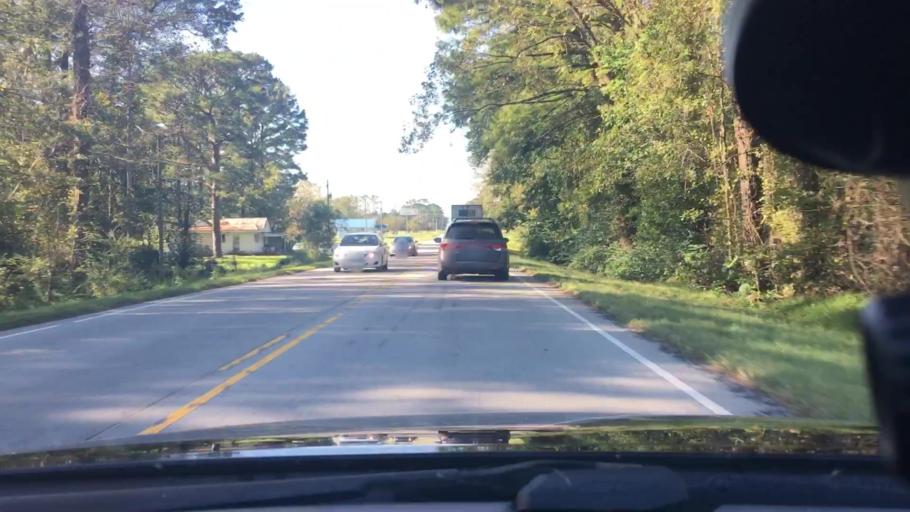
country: US
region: North Carolina
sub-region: Craven County
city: Vanceboro
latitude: 35.2688
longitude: -77.1097
